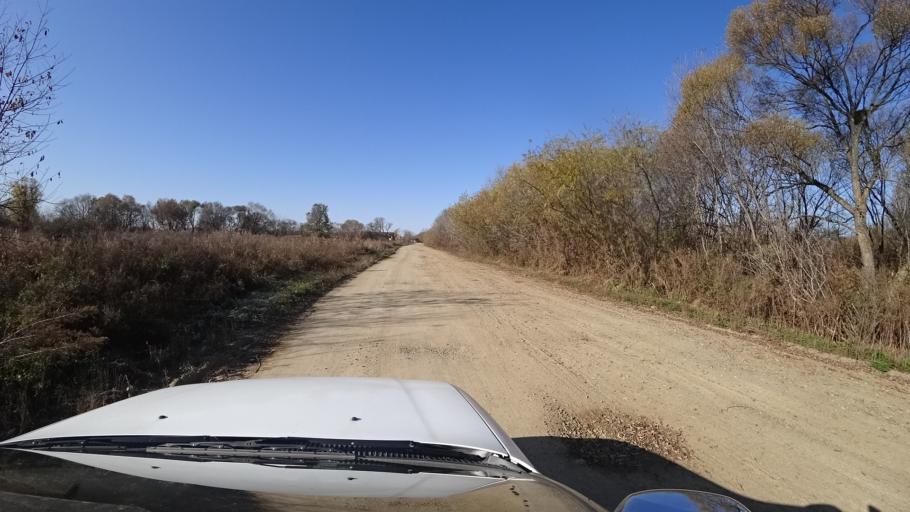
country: RU
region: Primorskiy
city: Dal'nerechensk
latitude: 45.9070
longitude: 133.8052
